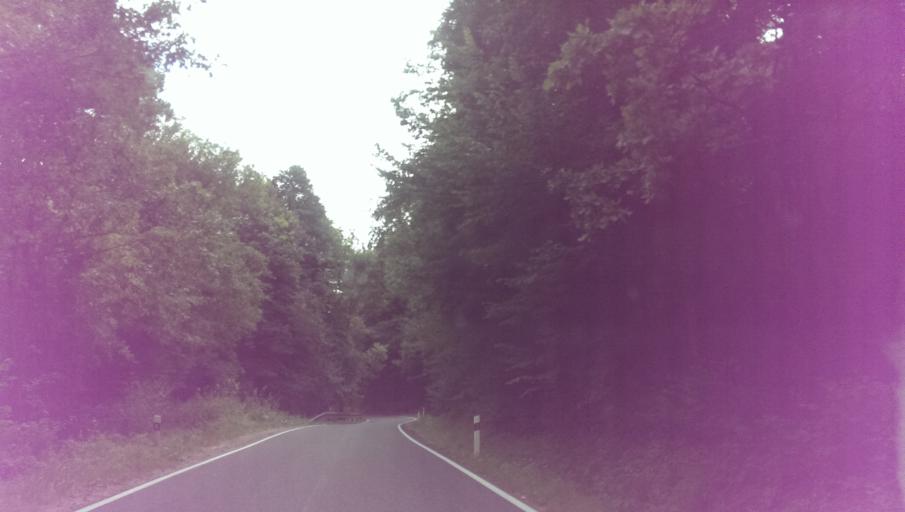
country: CZ
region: South Moravian
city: Velka nad Velickou
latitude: 48.8792
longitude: 17.5862
